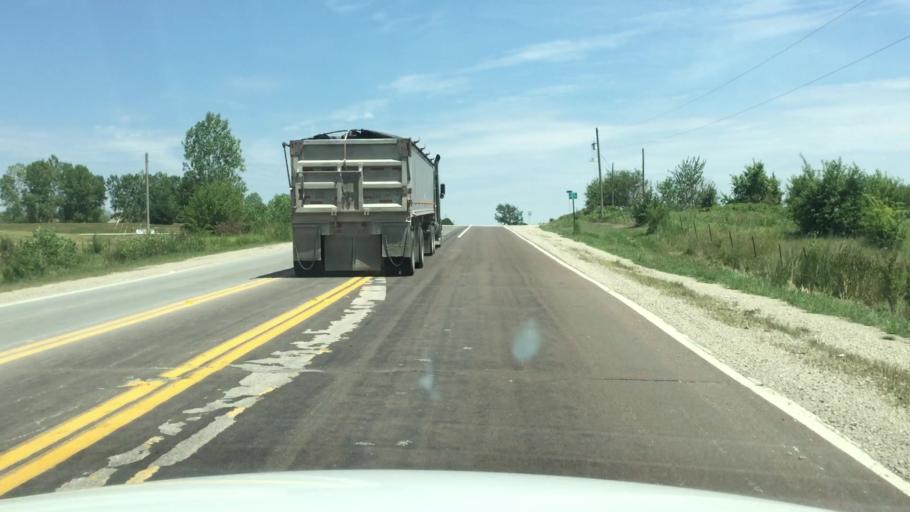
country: US
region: Kansas
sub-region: Shawnee County
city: Topeka
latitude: 38.9859
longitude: -95.5020
